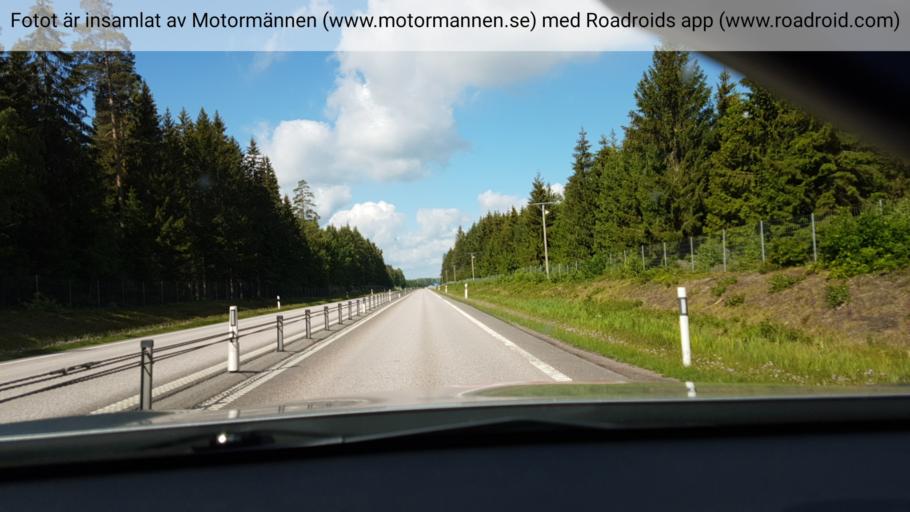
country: SE
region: Vaestra Goetaland
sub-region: Lidkopings Kommun
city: Vinninga
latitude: 58.3513
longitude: 13.3049
